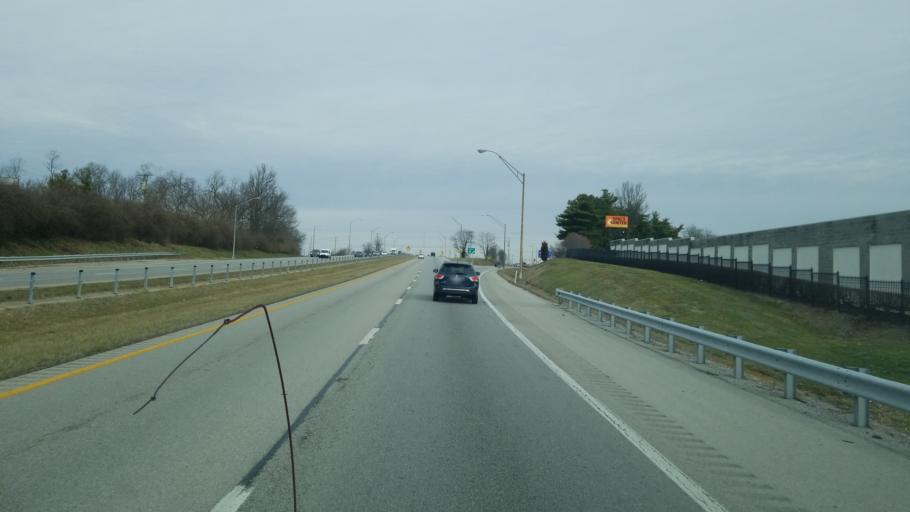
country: US
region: Kentucky
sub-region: Fayette County
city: Lexington
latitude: 38.0081
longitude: -84.4600
